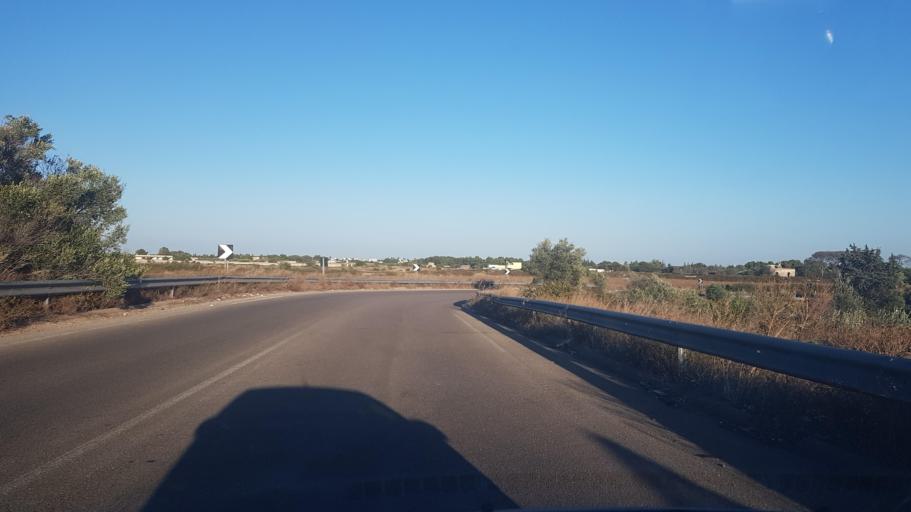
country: IT
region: Apulia
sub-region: Provincia di Lecce
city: Merine
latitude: 40.3426
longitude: 18.2030
